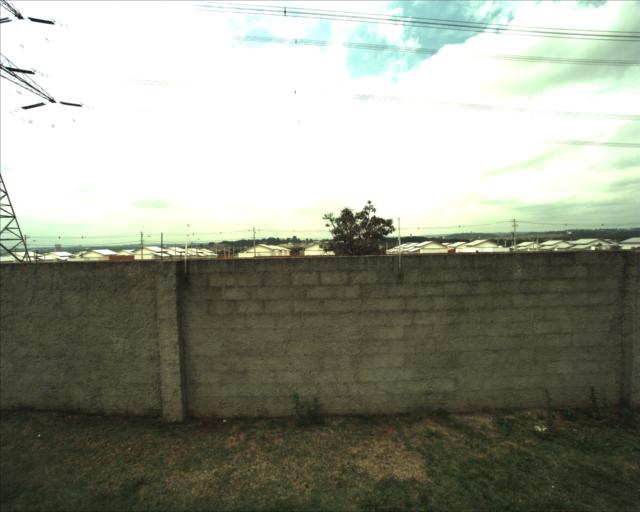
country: BR
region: Sao Paulo
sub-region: Sorocaba
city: Sorocaba
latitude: -23.4540
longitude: -47.3854
